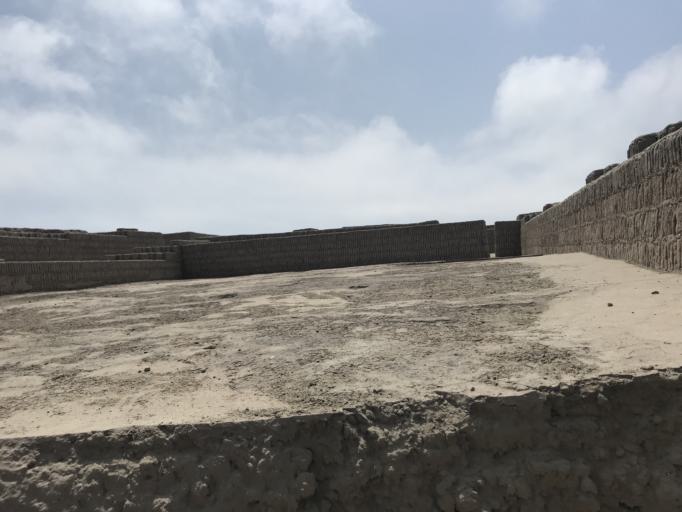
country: PE
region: Lima
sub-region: Lima
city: San Isidro
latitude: -12.1111
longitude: -77.0336
